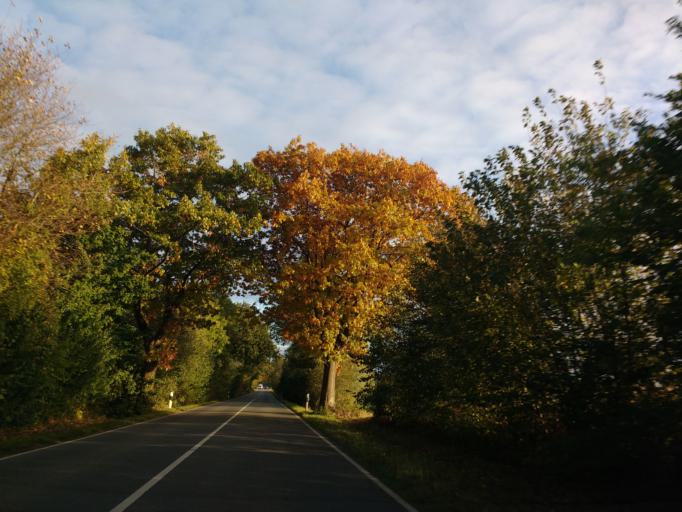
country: DE
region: Schleswig-Holstein
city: Schonwalde am Bungsberg
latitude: 54.1665
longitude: 10.7925
